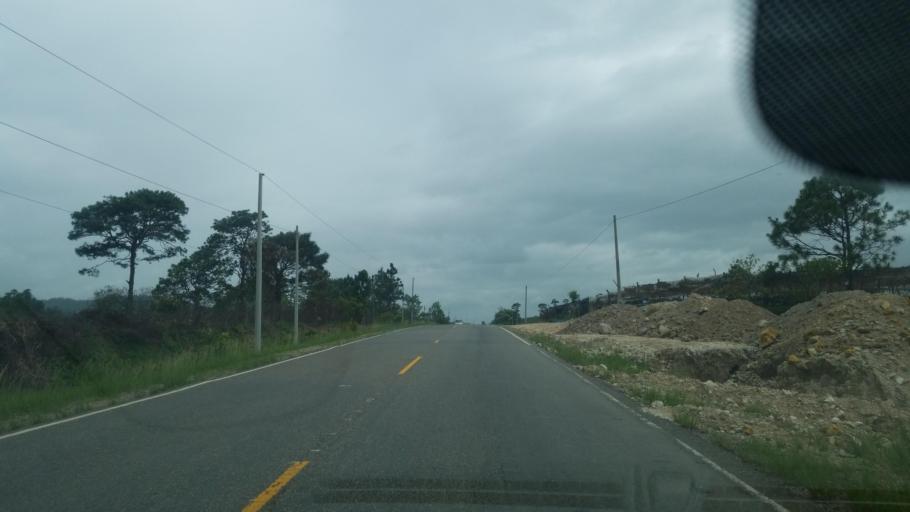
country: HN
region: Ocotepeque
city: Lucerna
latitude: 14.5734
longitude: -88.9301
